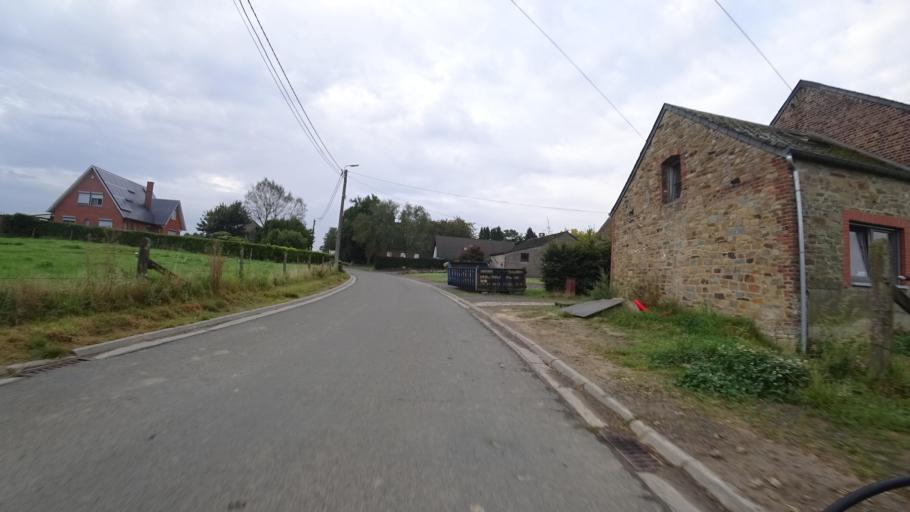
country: BE
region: Wallonia
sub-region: Province du Brabant Wallon
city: Perwez
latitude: 50.5583
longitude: 4.8054
